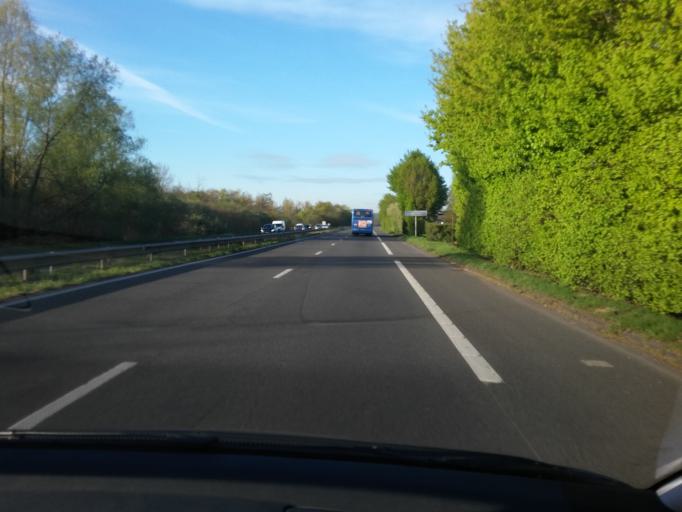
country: FR
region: Picardie
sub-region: Departement de l'Oise
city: Lacroix-Saint-Ouen
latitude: 49.3692
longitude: 2.7775
